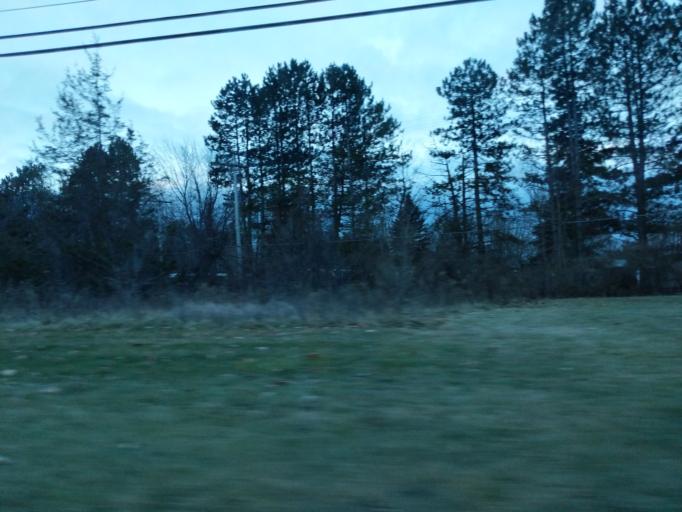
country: US
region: Michigan
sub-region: Lapeer County
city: Almont
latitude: 42.9279
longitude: -83.0493
